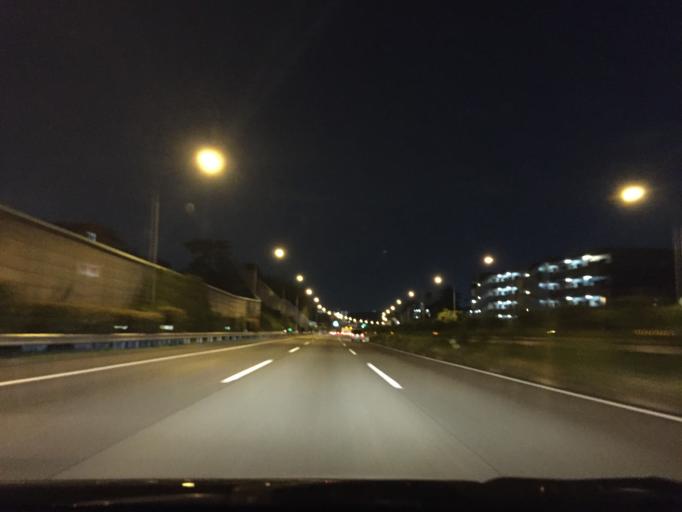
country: JP
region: Tokyo
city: Chofugaoka
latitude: 35.5760
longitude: 139.5644
